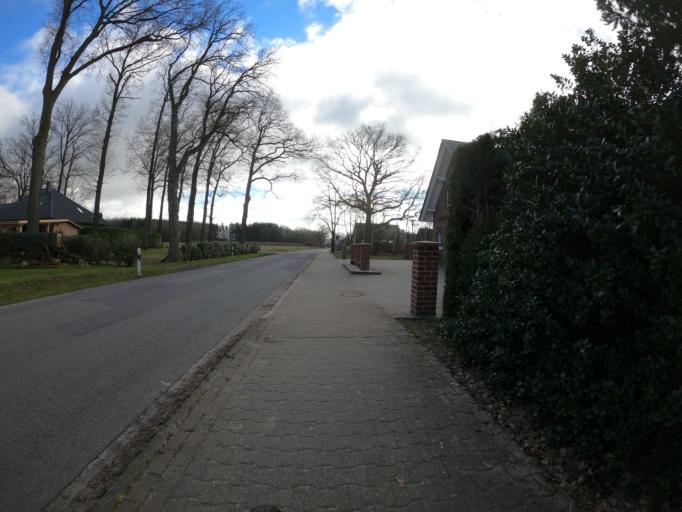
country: DE
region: Lower Saxony
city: Dohren
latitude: 52.6705
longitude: 7.5768
